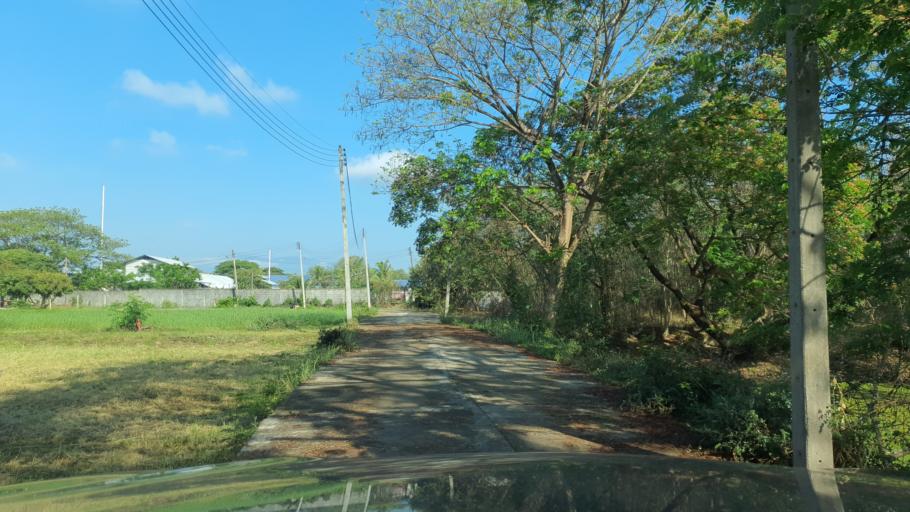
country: TH
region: Chiang Mai
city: San Kamphaeng
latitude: 18.7478
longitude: 99.1085
